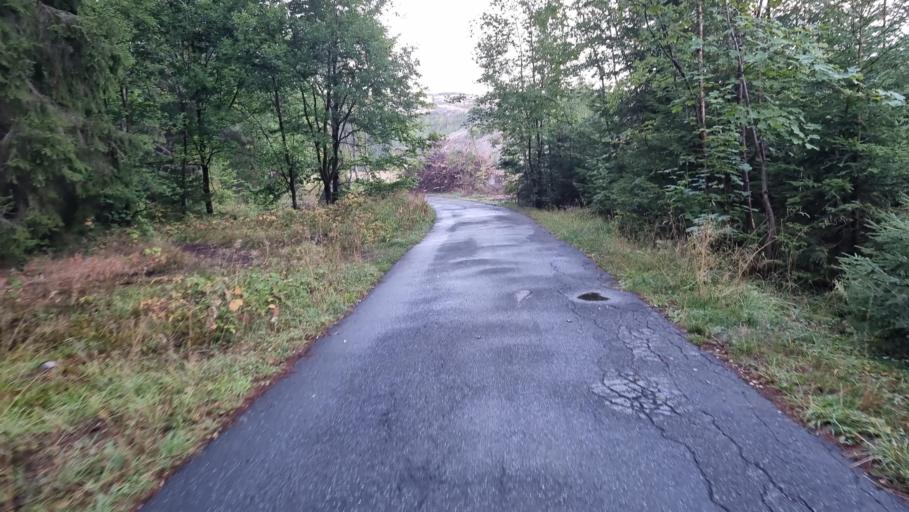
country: DE
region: Lower Saxony
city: Braunlage
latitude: 51.7360
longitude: 10.6123
